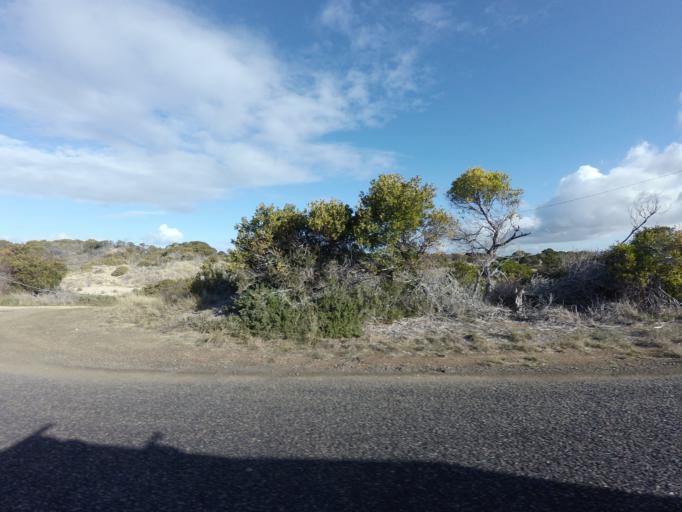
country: AU
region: Tasmania
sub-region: Break O'Day
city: St Helens
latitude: -42.0894
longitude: 148.1746
